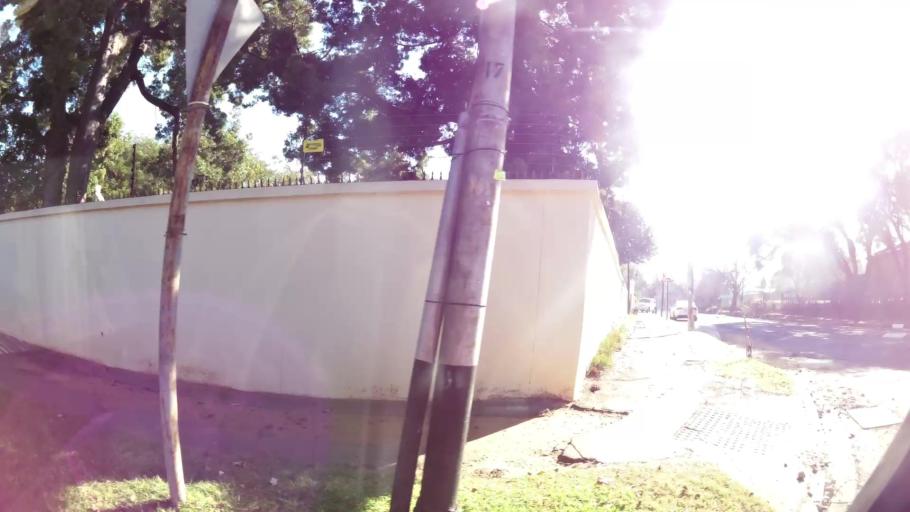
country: ZA
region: Gauteng
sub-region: City of Johannesburg Metropolitan Municipality
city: Johannesburg
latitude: -26.1236
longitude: 28.0229
